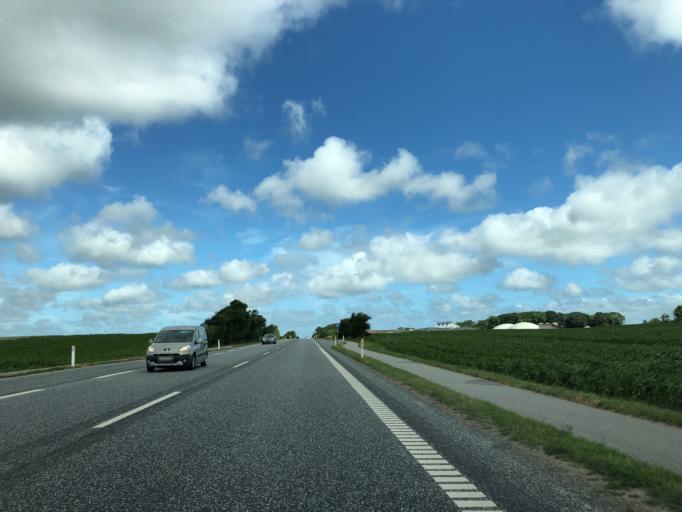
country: DK
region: Central Jutland
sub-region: Holstebro Kommune
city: Holstebro
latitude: 56.4222
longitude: 8.6006
